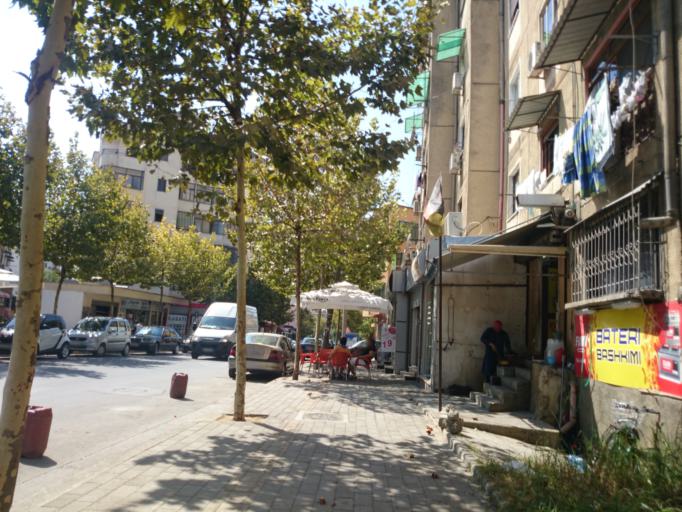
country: AL
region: Tirane
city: Tirana
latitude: 41.3277
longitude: 19.8309
